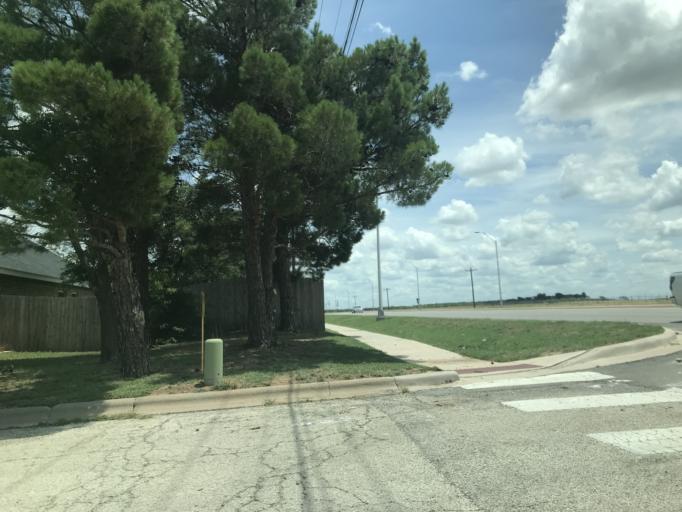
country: US
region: Texas
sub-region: Taylor County
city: Abilene
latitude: 32.4847
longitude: -99.6852
